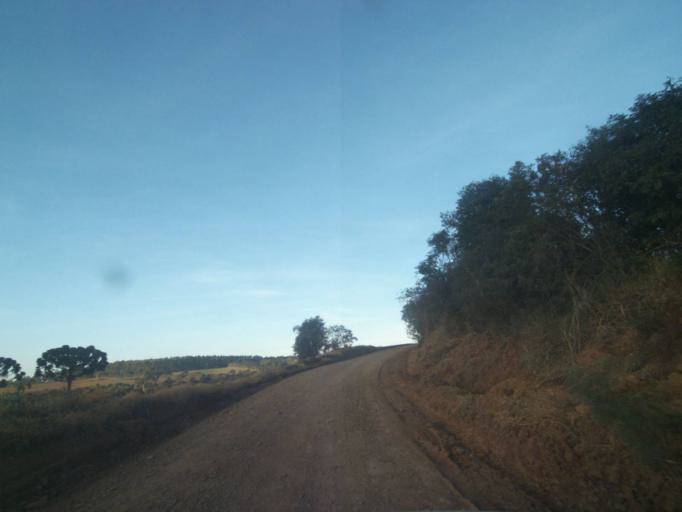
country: BR
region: Parana
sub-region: Tibagi
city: Tibagi
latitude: -24.5227
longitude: -50.5042
